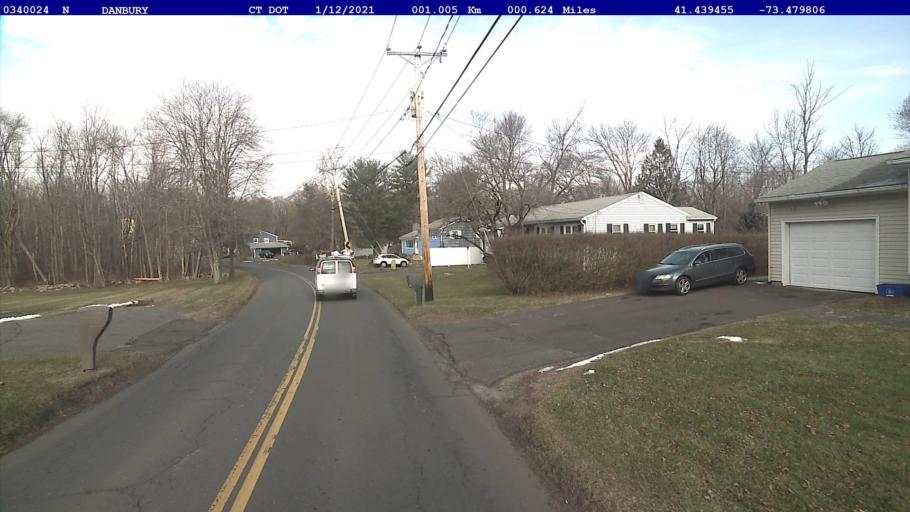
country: US
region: Connecticut
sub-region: Fairfield County
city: Danbury
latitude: 41.4395
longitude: -73.4799
